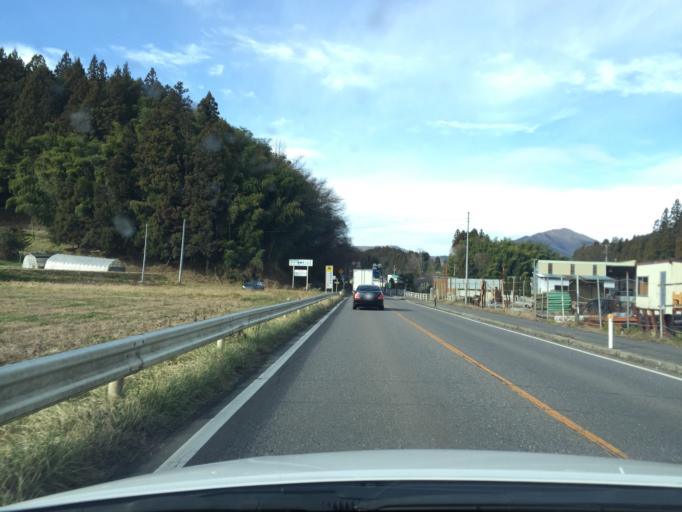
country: JP
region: Fukushima
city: Ishikawa
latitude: 37.2343
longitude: 140.5747
